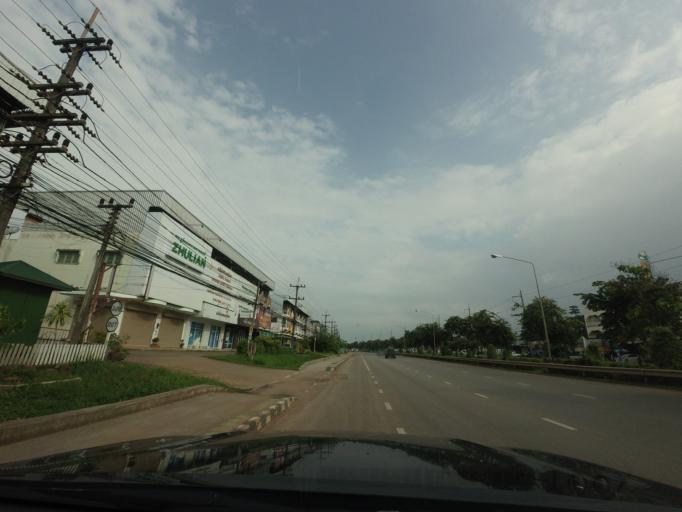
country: TH
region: Nong Khai
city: Nong Khai
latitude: 17.8608
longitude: 102.7491
